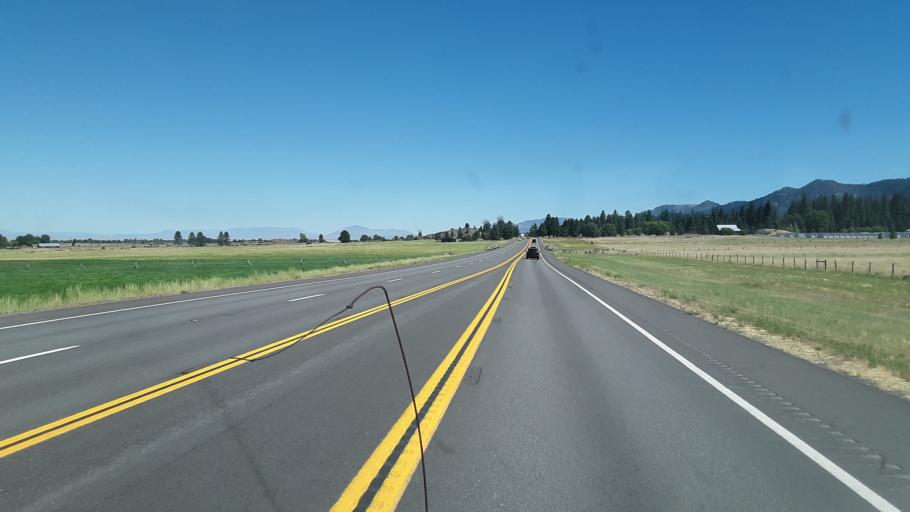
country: US
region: California
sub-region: Lassen County
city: Janesville
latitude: 40.3128
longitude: -120.5369
